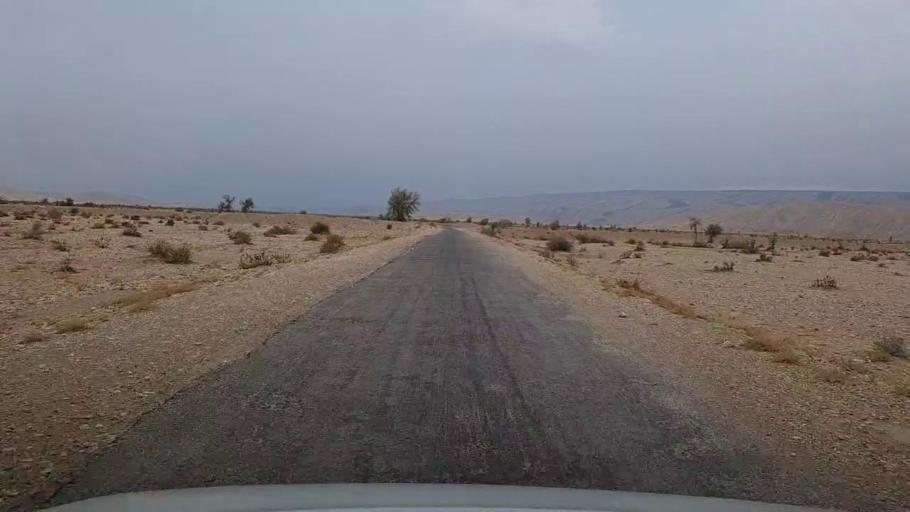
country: PK
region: Sindh
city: Sehwan
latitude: 26.2583
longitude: 67.7218
